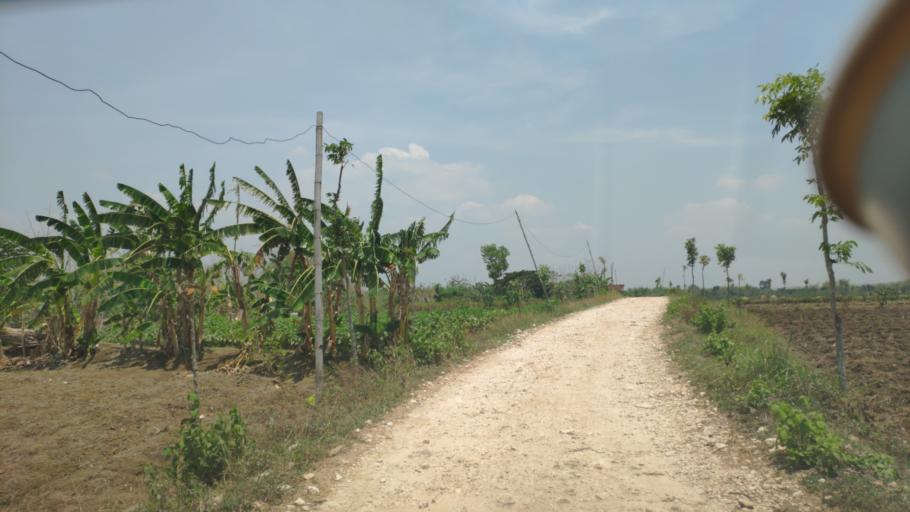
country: ID
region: Central Java
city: Karangtengah
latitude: -7.0422
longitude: 111.3195
